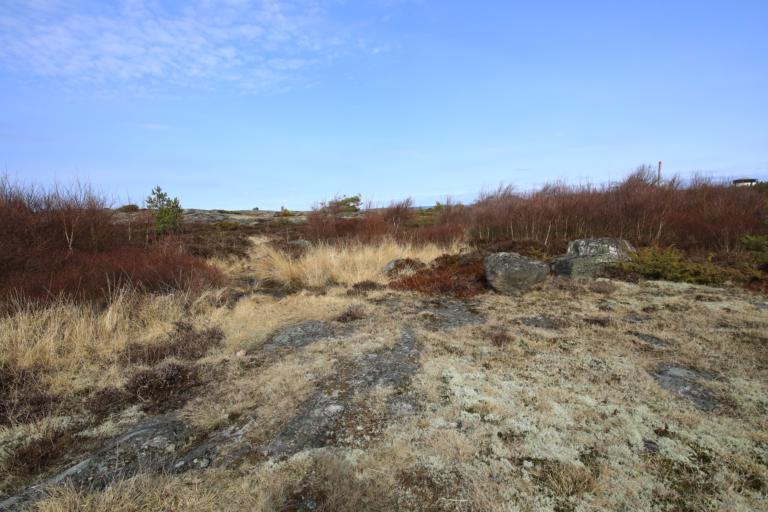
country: SE
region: Halland
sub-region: Kungsbacka Kommun
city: Frillesas
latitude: 57.2555
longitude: 12.0963
